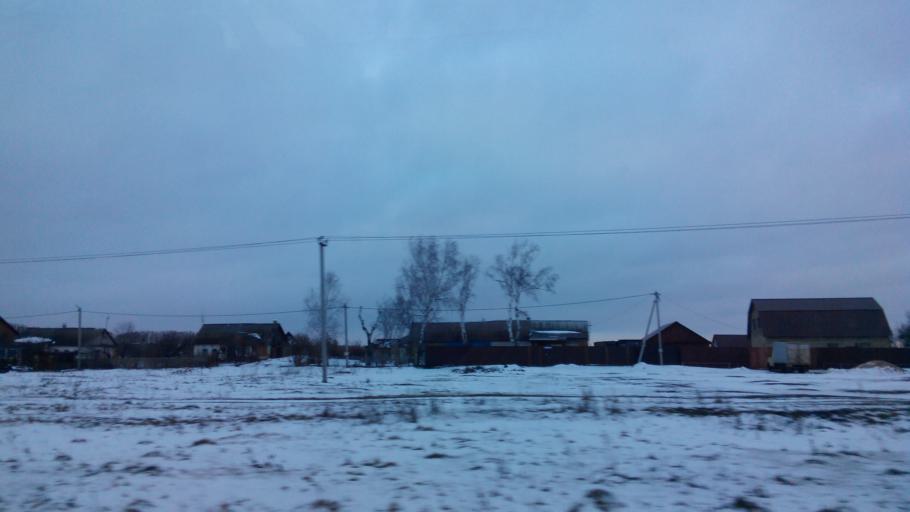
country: RU
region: Tula
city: Mayskiy
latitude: 53.9768
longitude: 38.2370
